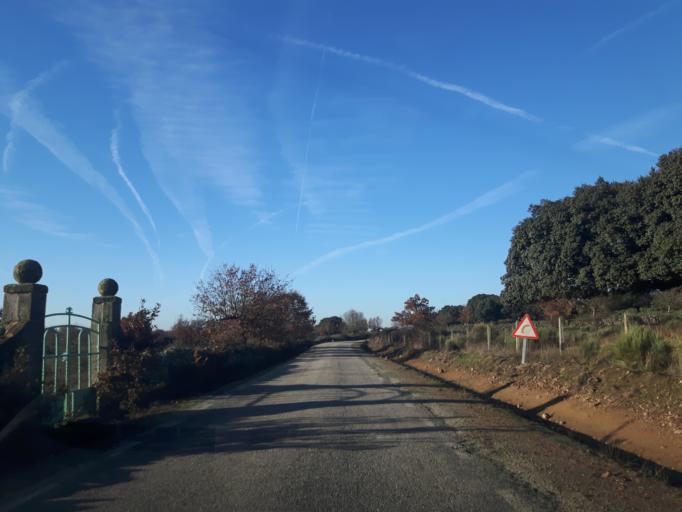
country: ES
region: Castille and Leon
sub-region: Provincia de Salamanca
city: Cerralbo
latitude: 40.9448
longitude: -6.6120
